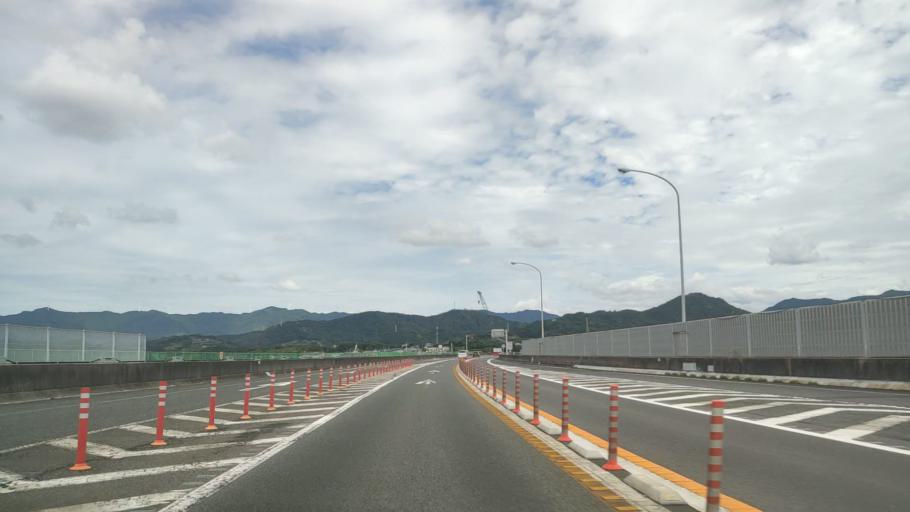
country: JP
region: Wakayama
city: Gobo
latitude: 33.9004
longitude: 135.1859
